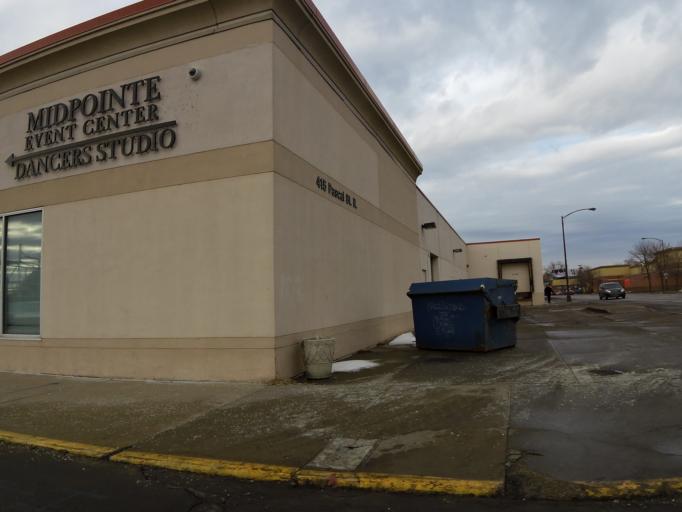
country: US
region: Minnesota
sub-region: Ramsey County
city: Falcon Heights
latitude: 44.9537
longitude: -93.1620
